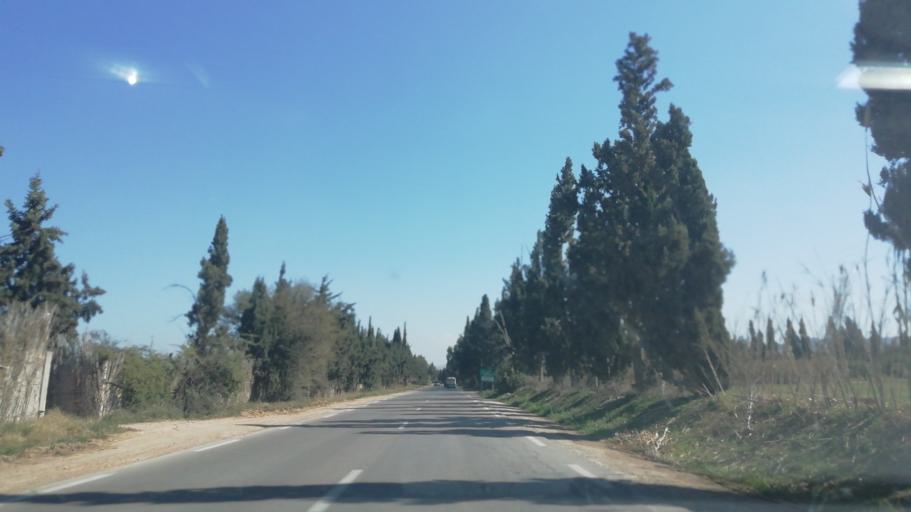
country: DZ
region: Mascara
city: Sig
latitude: 35.5723
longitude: -0.0234
